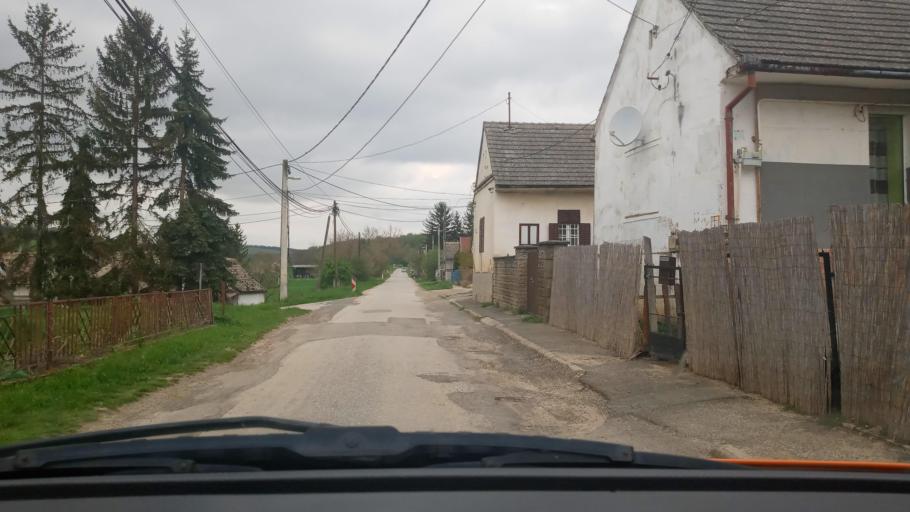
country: HU
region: Baranya
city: Boly
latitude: 46.0083
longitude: 18.5479
